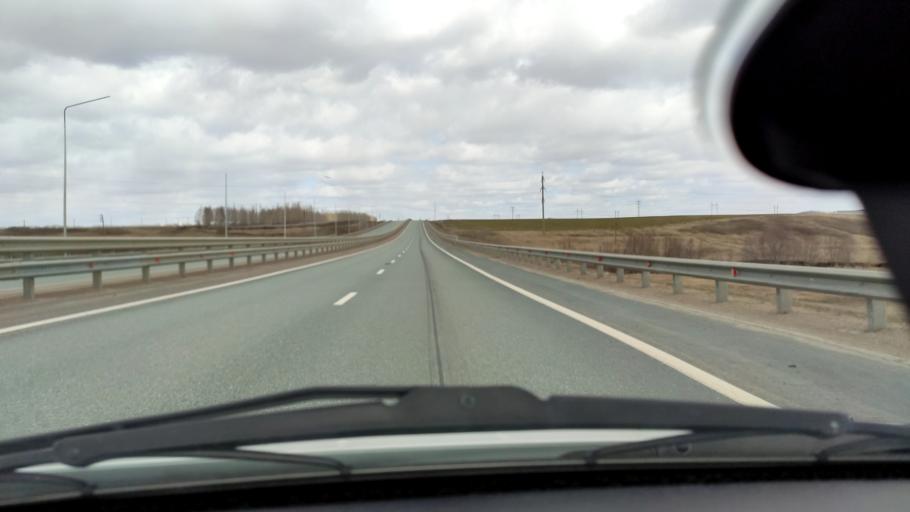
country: RU
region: Bashkortostan
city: Tolbazy
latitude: 54.2285
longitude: 55.8820
